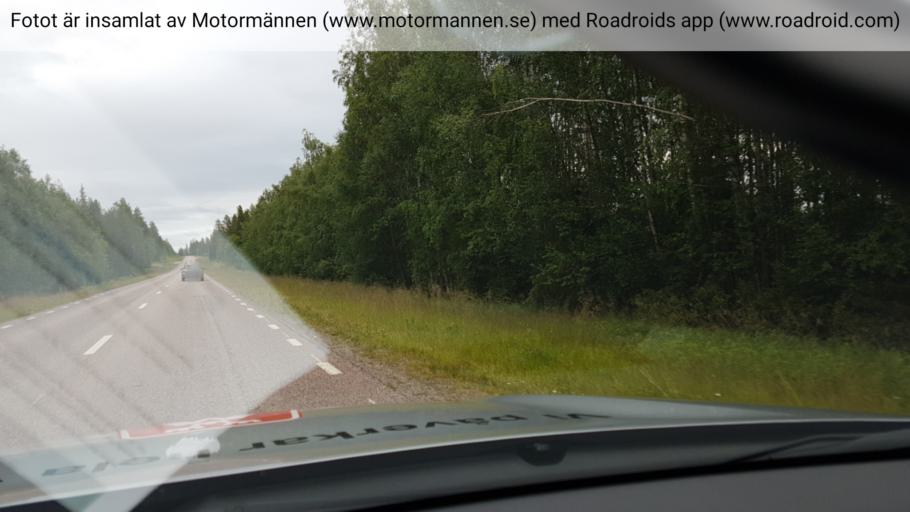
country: SE
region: Norrbotten
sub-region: Gallivare Kommun
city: Gaellivare
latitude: 67.0510
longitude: 21.6030
